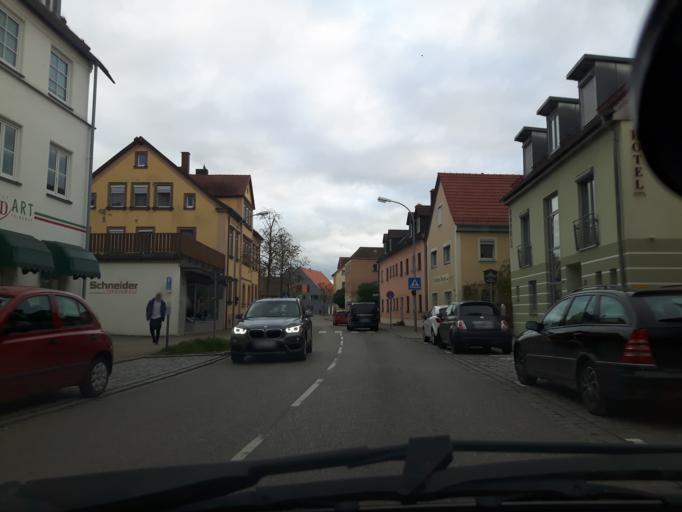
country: DE
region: Bavaria
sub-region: Regierungsbezirk Mittelfranken
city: Gunzenhausen
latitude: 49.1116
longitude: 10.7559
